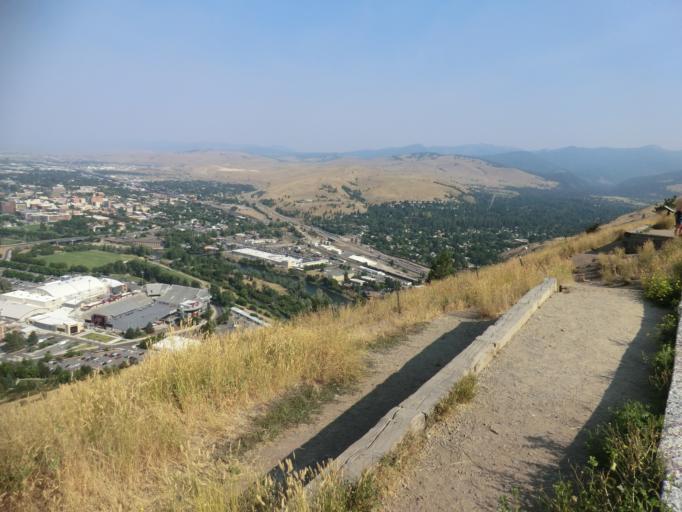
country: US
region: Montana
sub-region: Missoula County
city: Missoula
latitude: 46.8593
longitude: -113.9760
